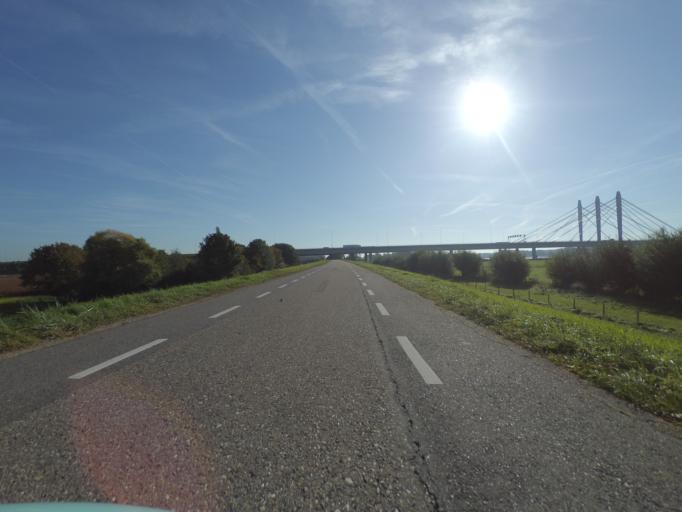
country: NL
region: Gelderland
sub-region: Gemeente Overbetuwe
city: Andelst
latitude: 51.8899
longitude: 5.7354
